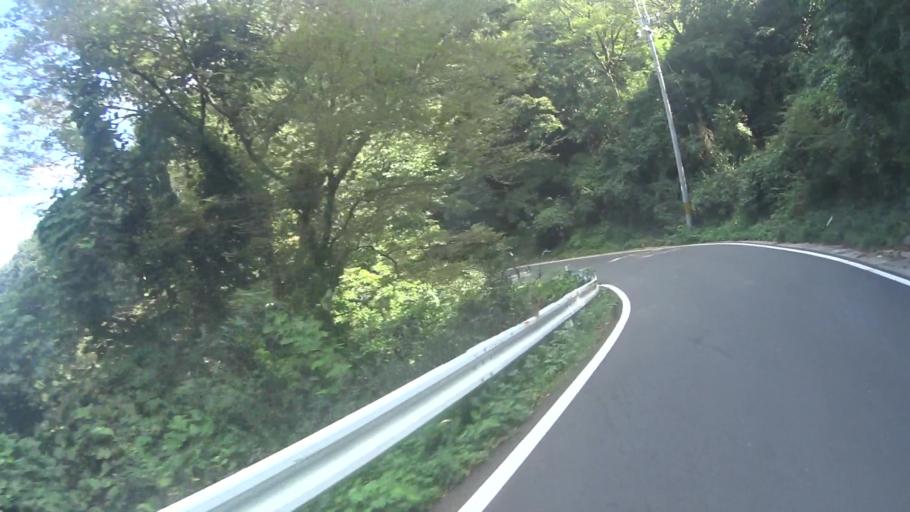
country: JP
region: Kyoto
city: Miyazu
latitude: 35.7480
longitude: 135.2483
